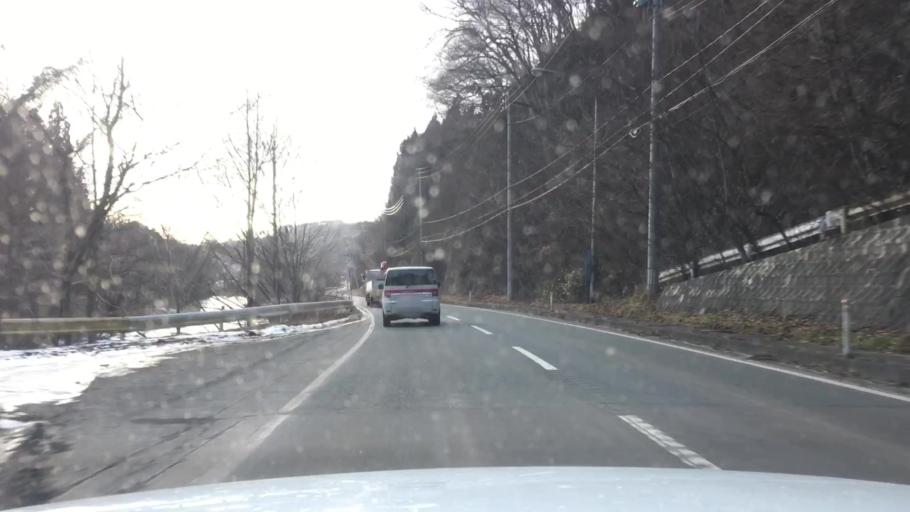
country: JP
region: Iwate
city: Morioka-shi
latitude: 39.6769
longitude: 141.2209
